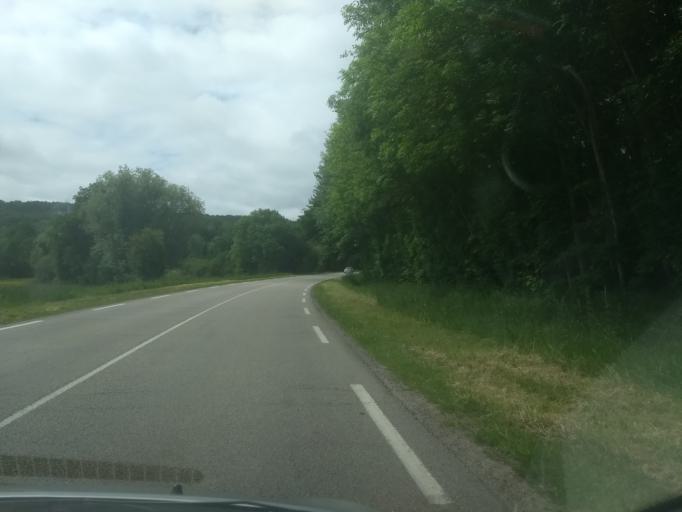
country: FR
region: Lower Normandy
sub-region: Departement de l'Orne
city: Remalard
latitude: 48.4244
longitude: 0.7837
